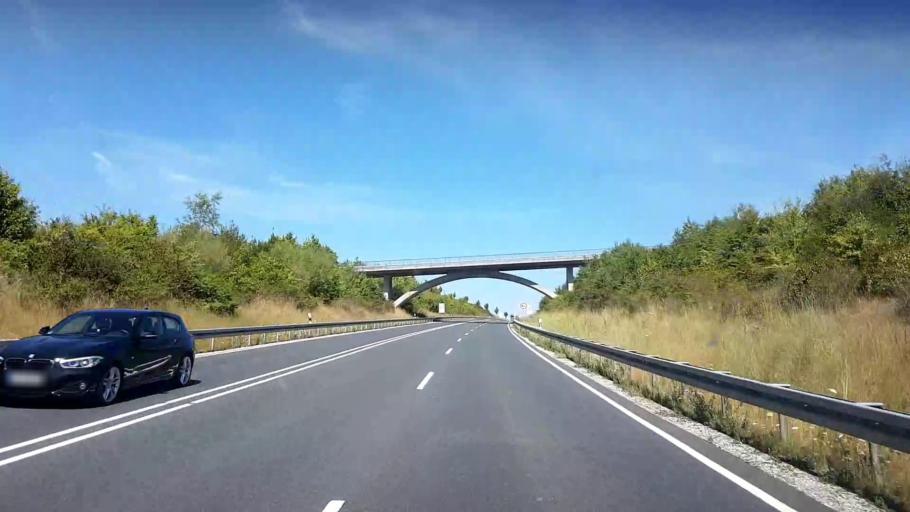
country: DE
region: Bavaria
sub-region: Upper Franconia
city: Untersiemau
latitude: 50.1679
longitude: 10.9954
